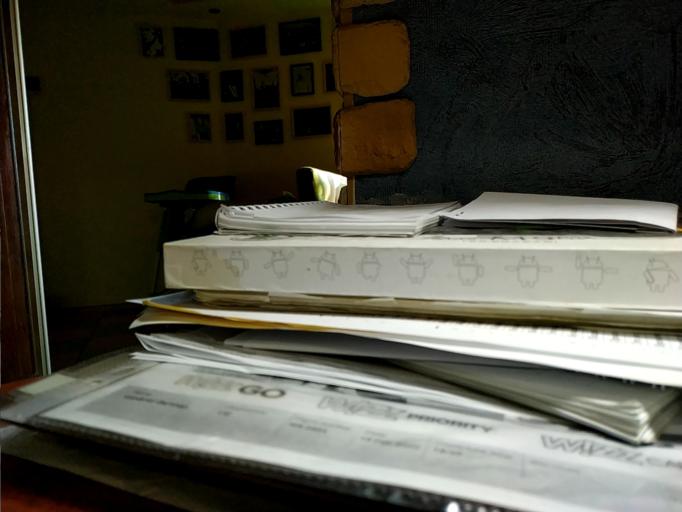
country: RU
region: Novgorod
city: Kholm
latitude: 57.1137
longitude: 31.4837
